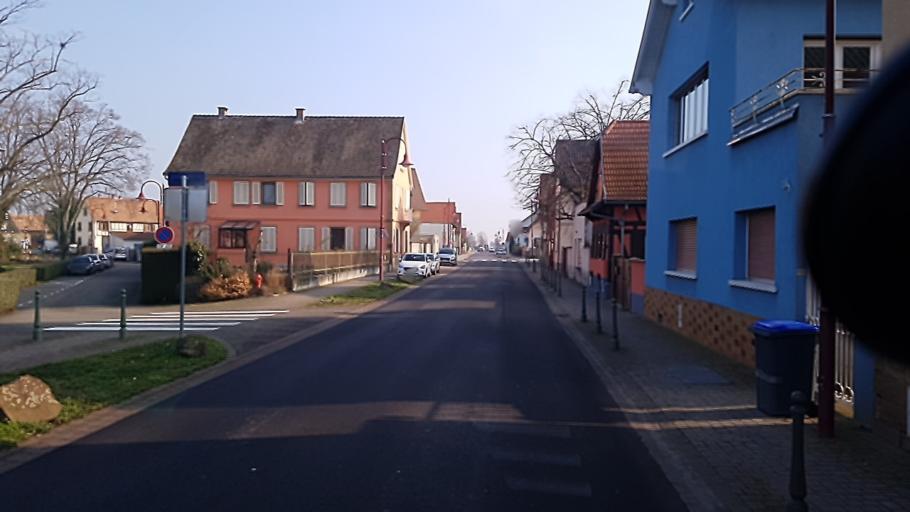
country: FR
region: Alsace
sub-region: Departement du Bas-Rhin
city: Entzheim
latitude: 48.5348
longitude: 7.6373
